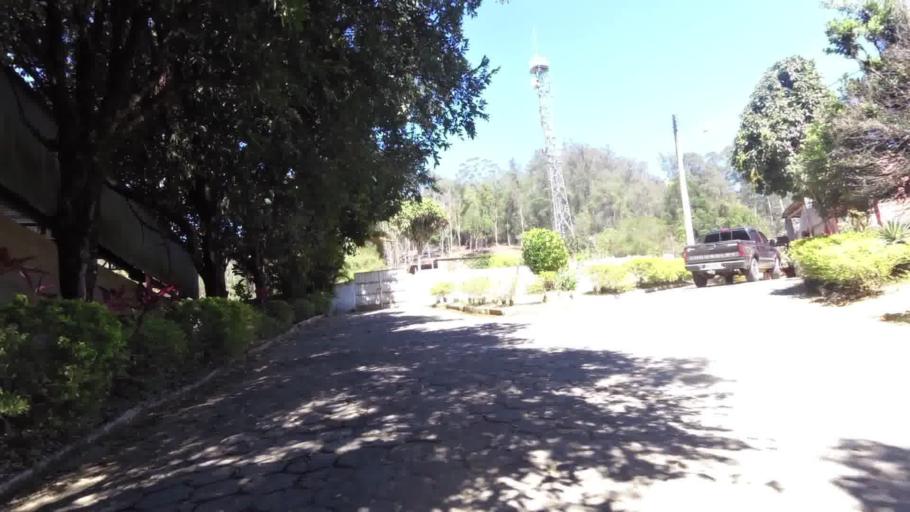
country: BR
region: Espirito Santo
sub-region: Vargem Alta
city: Vargem Alta
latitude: -20.6765
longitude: -41.0135
